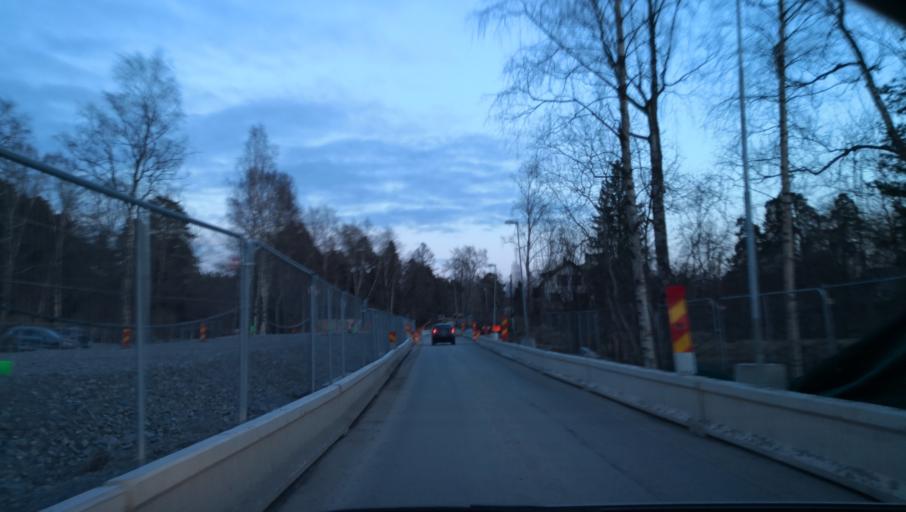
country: SE
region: Stockholm
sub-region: Nacka Kommun
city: Kummelnas
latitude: 59.3462
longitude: 18.2902
